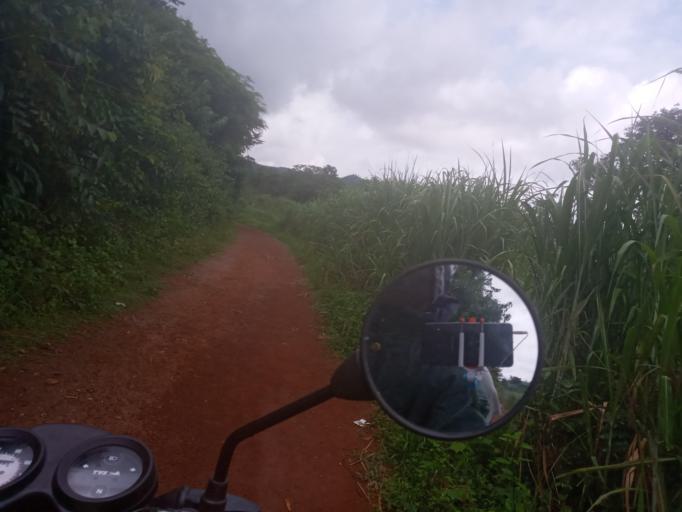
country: SL
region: Northern Province
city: Bumbuna
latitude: 8.9213
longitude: -11.7425
